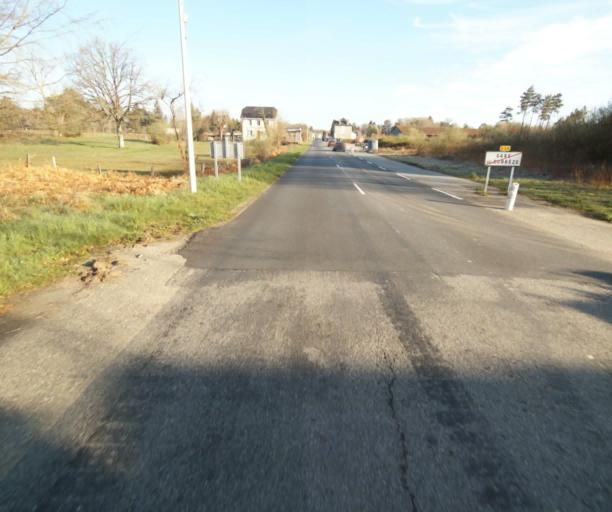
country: FR
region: Limousin
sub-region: Departement de la Correze
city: Correze
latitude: 45.3364
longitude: 1.8768
